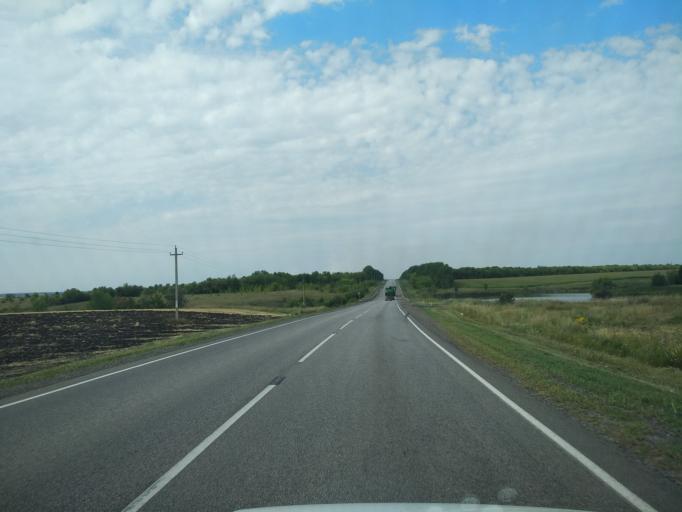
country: RU
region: Lipetsk
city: Dobrinka
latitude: 51.8942
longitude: 40.4487
